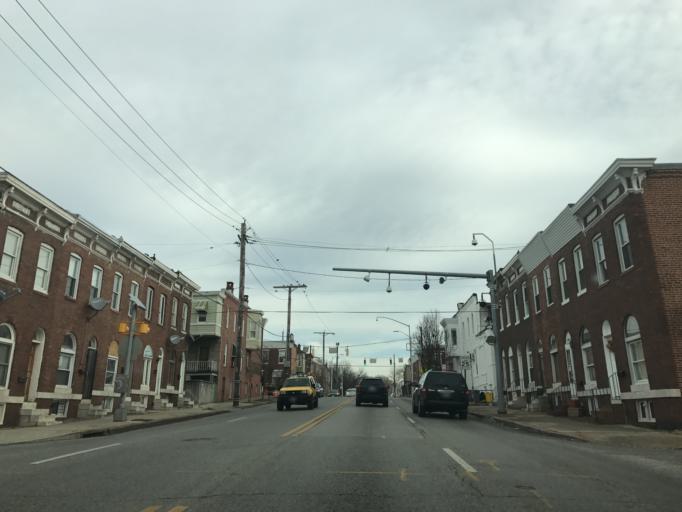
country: US
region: Maryland
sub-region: City of Baltimore
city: Baltimore
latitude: 39.2956
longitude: -76.5775
